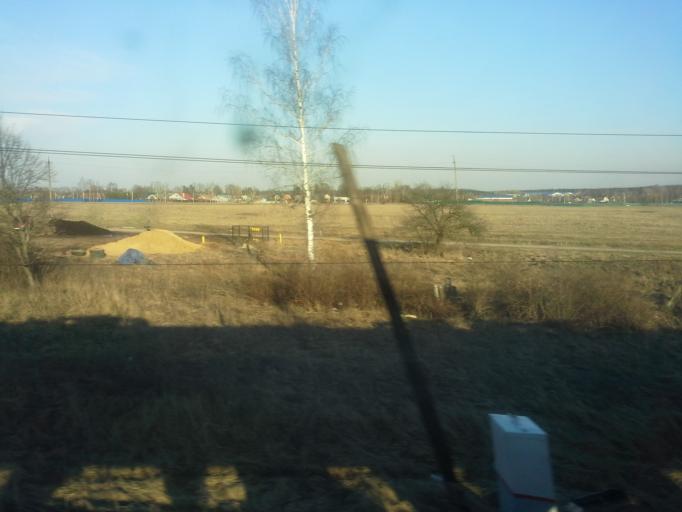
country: RU
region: Moskovskaya
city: Nekrasovskiy
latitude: 56.0837
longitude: 37.5008
